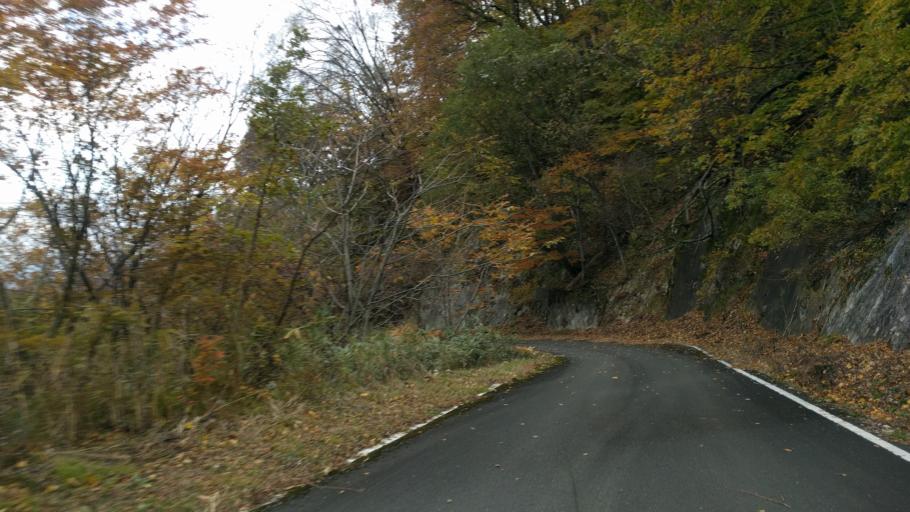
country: JP
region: Fukushima
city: Kitakata
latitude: 37.3862
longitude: 139.7247
